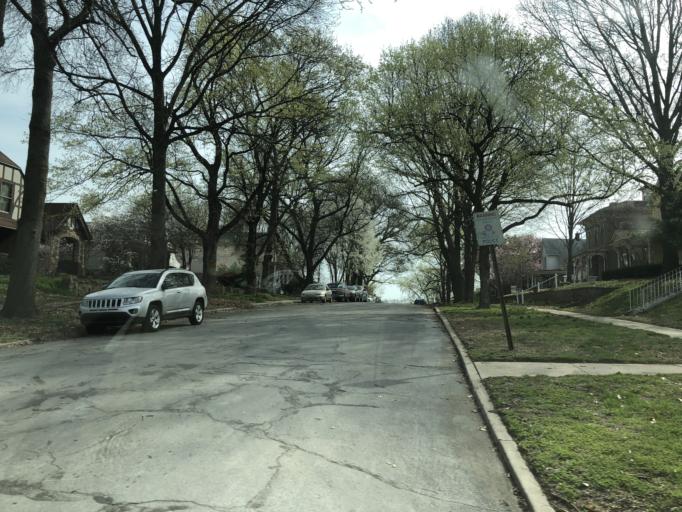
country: US
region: Kansas
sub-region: Leavenworth County
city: Leavenworth
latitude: 39.3123
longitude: -94.9173
